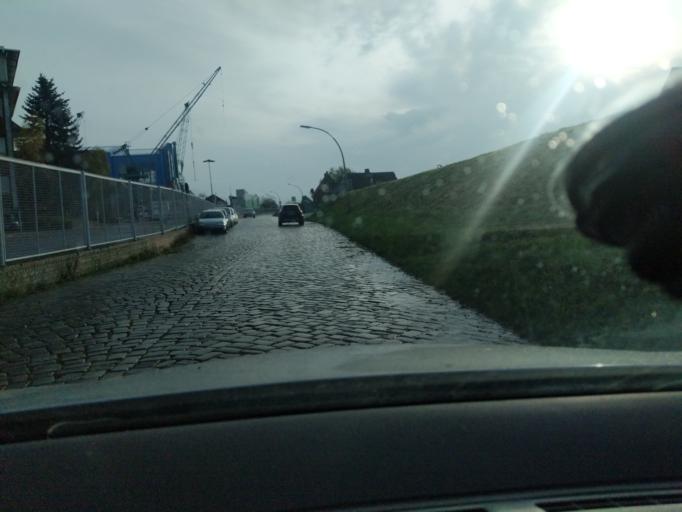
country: DE
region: Lower Saxony
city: Neu Wulmstorf
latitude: 53.5316
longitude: 9.7859
